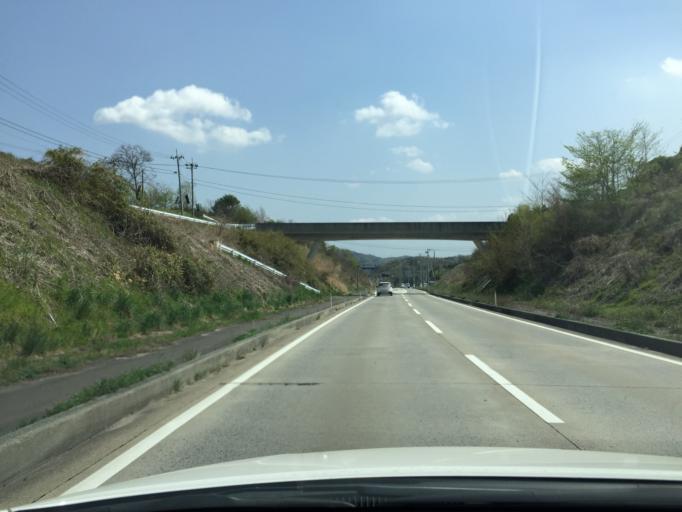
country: JP
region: Fukushima
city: Funehikimachi-funehiki
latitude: 37.4427
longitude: 140.5373
